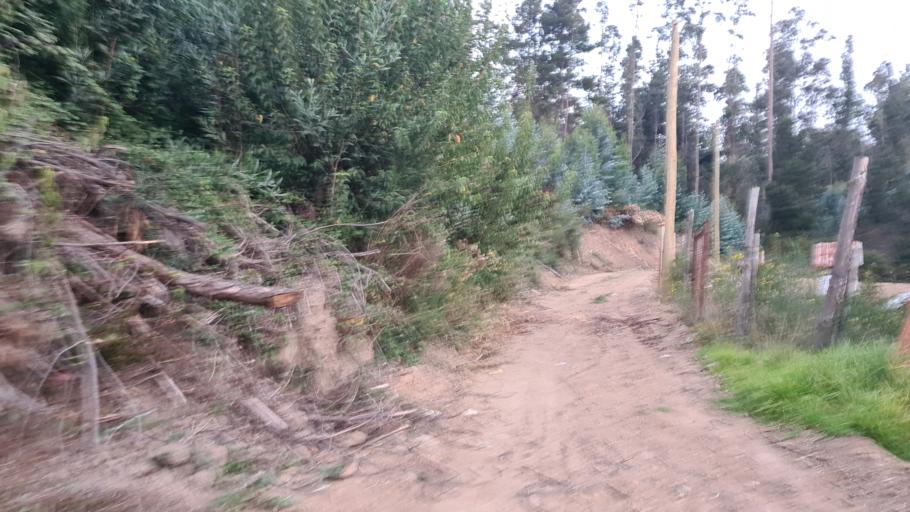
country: CL
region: Biobio
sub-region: Provincia de Concepcion
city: Penco
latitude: -36.7177
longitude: -72.9656
